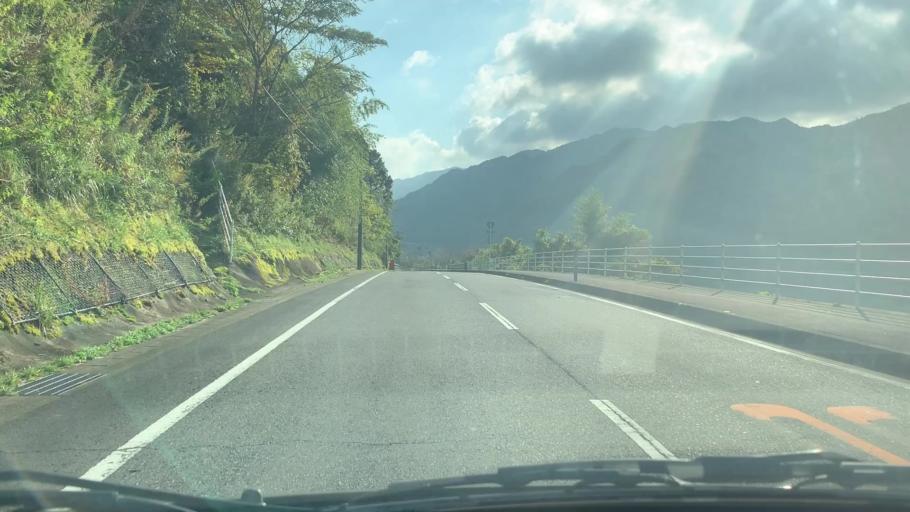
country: JP
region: Saga Prefecture
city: Kashima
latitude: 33.0384
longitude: 130.0712
